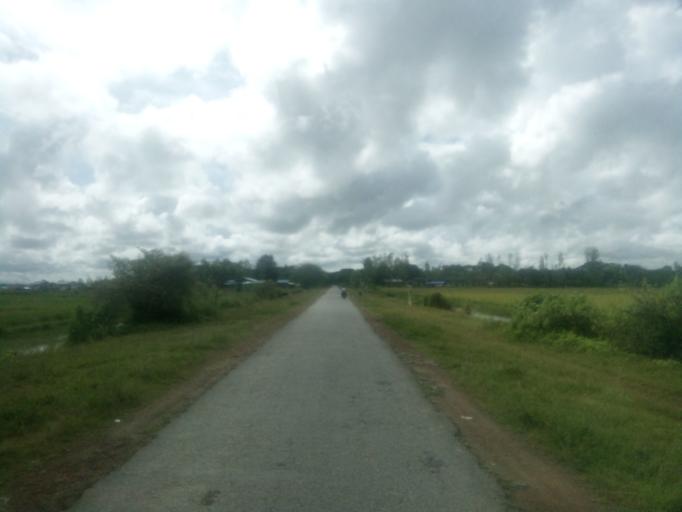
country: MM
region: Bago
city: Nyaunglebin
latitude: 17.9075
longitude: 96.5410
